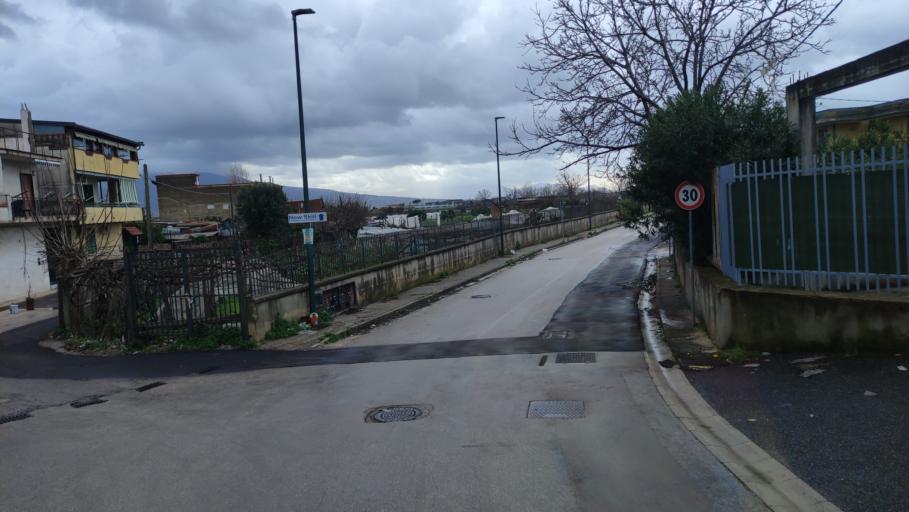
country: IT
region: Campania
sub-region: Provincia di Napoli
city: Casoria
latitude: 40.8936
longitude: 14.2938
